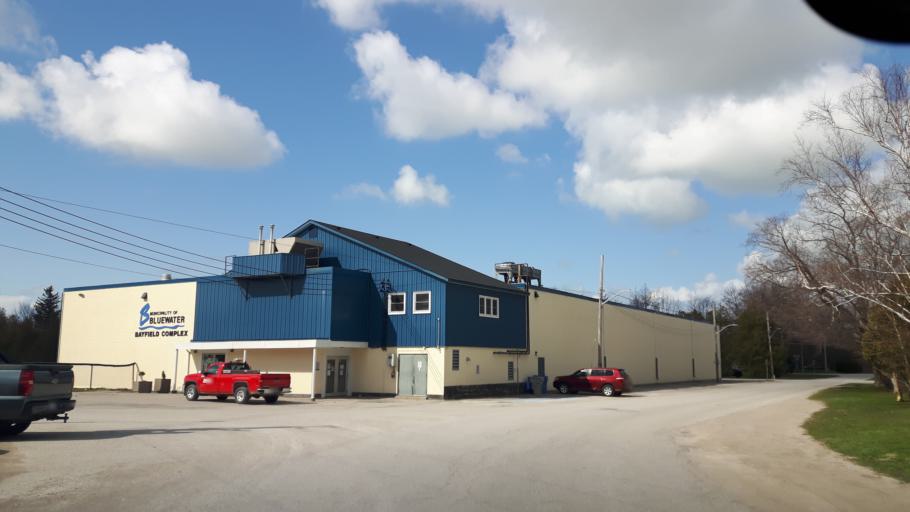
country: CA
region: Ontario
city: Bluewater
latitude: 43.5605
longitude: -81.6966
